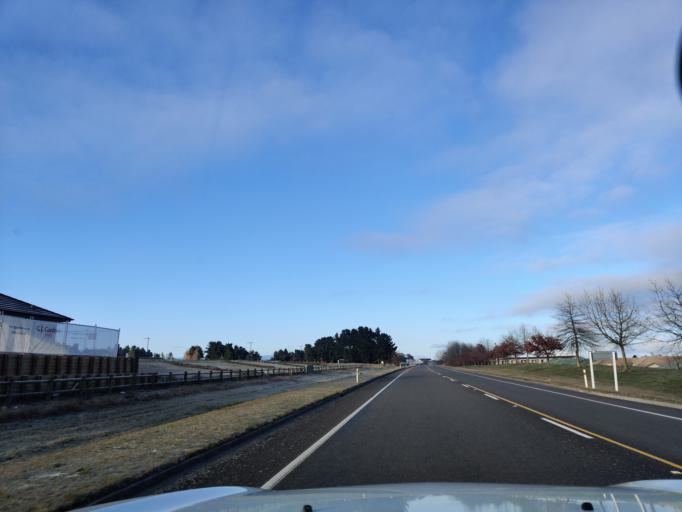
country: NZ
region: Waikato
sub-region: Taupo District
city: Taupo
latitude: -38.7298
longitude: 176.0741
